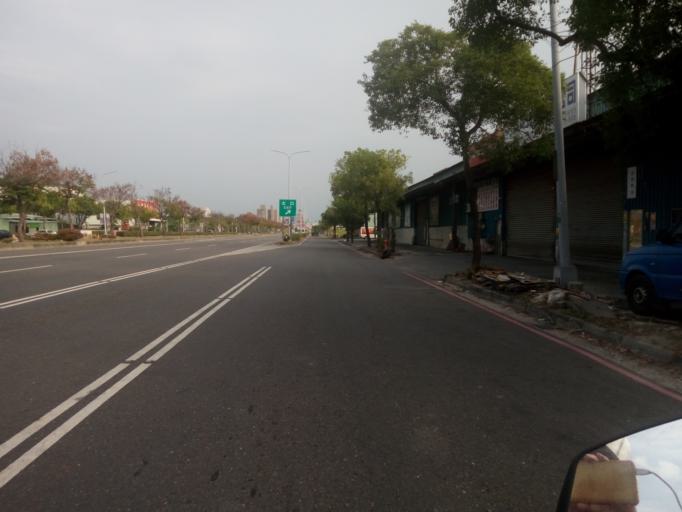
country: TW
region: Taiwan
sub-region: Chiayi
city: Jiayi Shi
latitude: 23.4832
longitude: 120.4157
